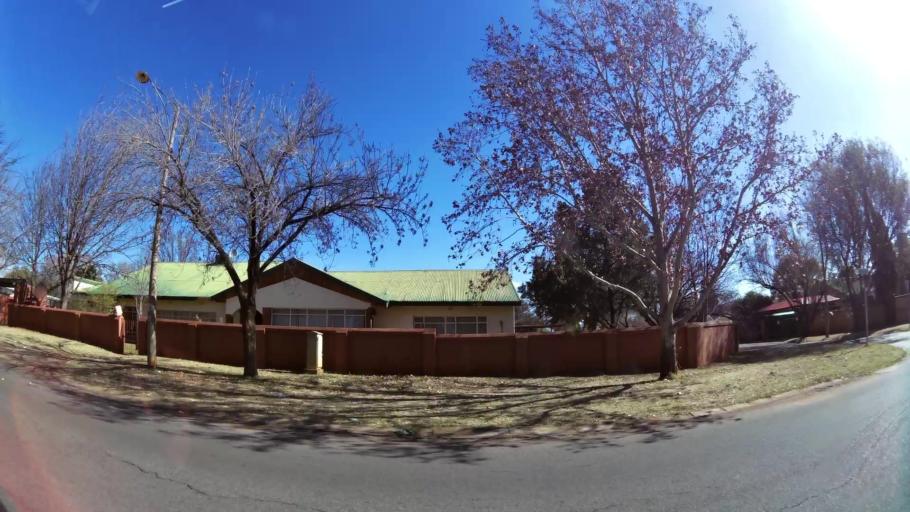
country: ZA
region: Gauteng
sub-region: West Rand District Municipality
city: Carletonville
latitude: -26.3465
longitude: 27.3869
